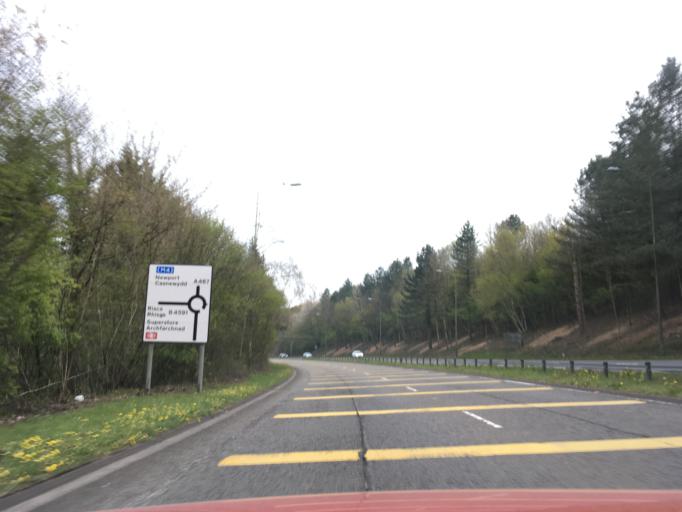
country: GB
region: Wales
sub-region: Caerphilly County Borough
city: Risca
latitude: 51.6016
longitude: -3.0974
